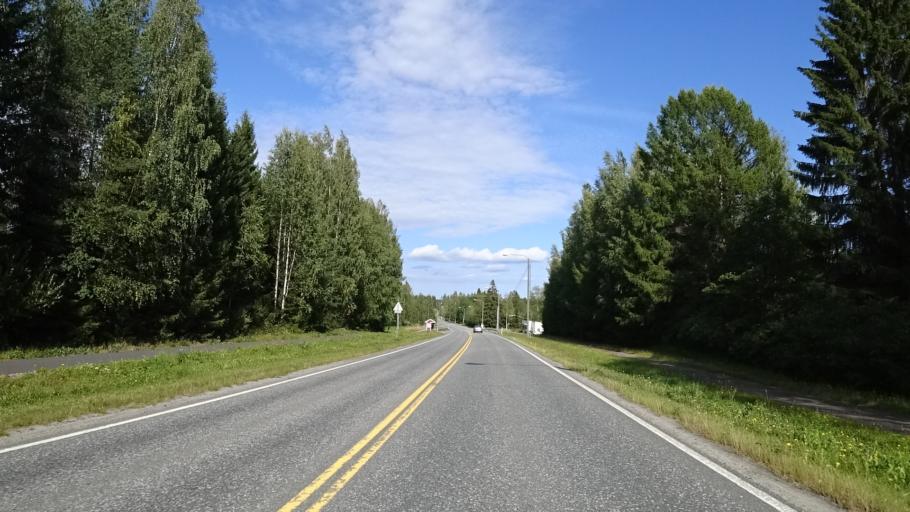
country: FI
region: North Karelia
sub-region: Joensuu
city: Eno
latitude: 62.7994
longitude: 30.1109
